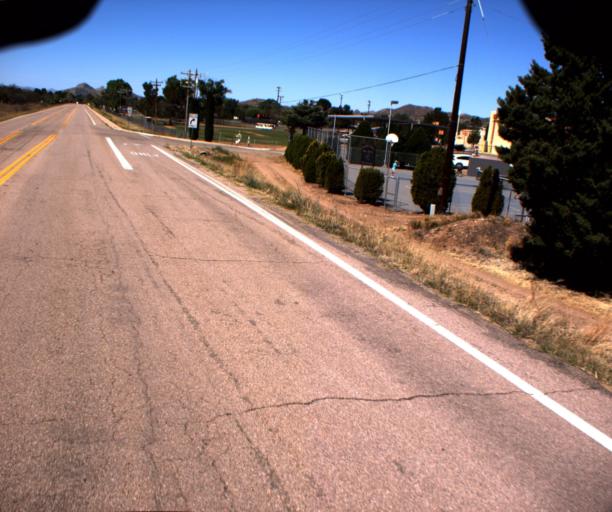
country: US
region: Arizona
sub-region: Santa Cruz County
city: Rio Rico
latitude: 31.5460
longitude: -110.7444
